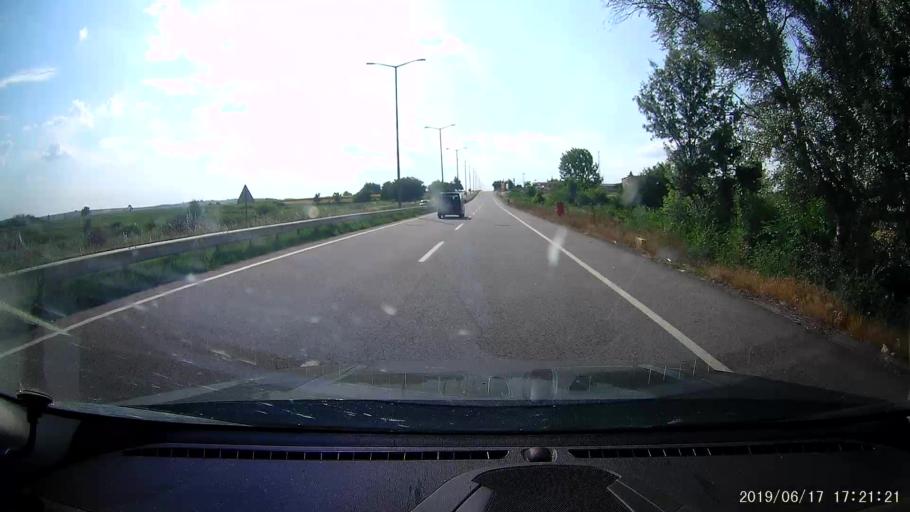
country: GR
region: East Macedonia and Thrace
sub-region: Nomos Evrou
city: Rizia
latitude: 41.7056
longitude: 26.3961
